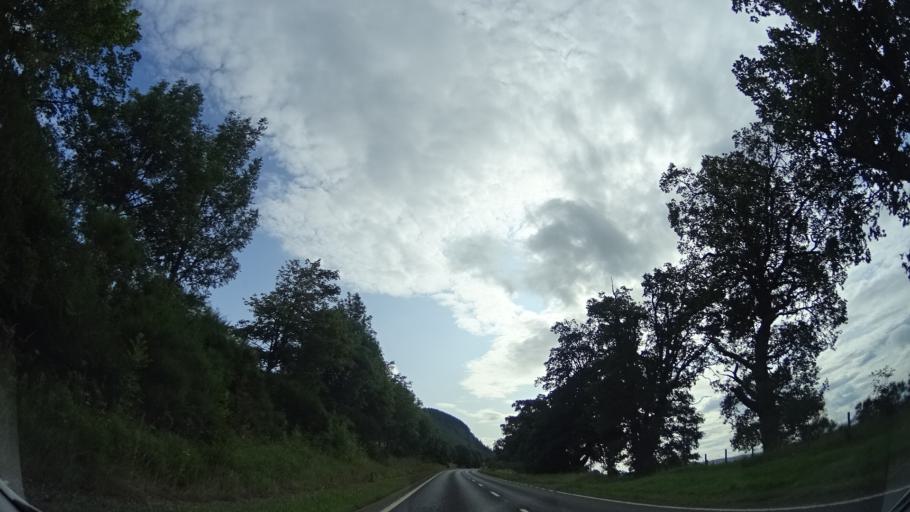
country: GB
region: Scotland
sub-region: Highland
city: Muir of Ord
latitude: 57.5584
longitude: -4.5334
